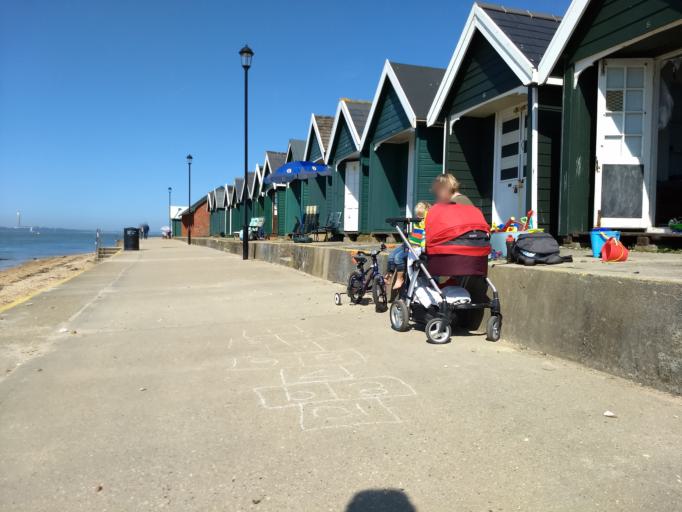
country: GB
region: England
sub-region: Isle of Wight
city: Gurnard
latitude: 50.7610
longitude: -1.3243
